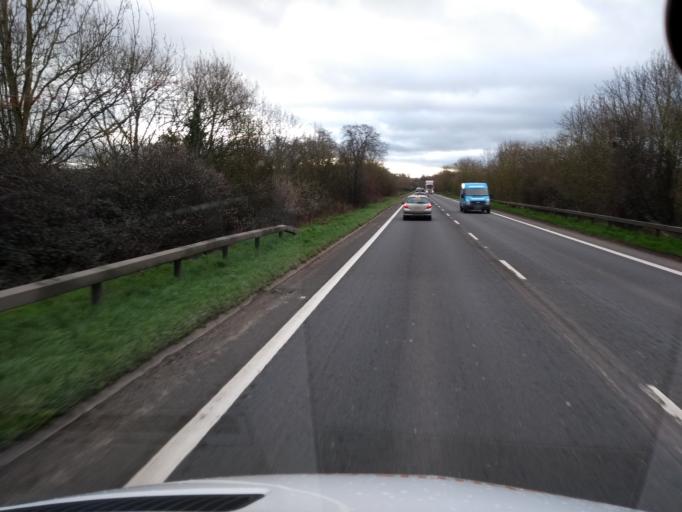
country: GB
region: England
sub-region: Somerset
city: Ilminster
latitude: 50.9375
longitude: -2.9462
